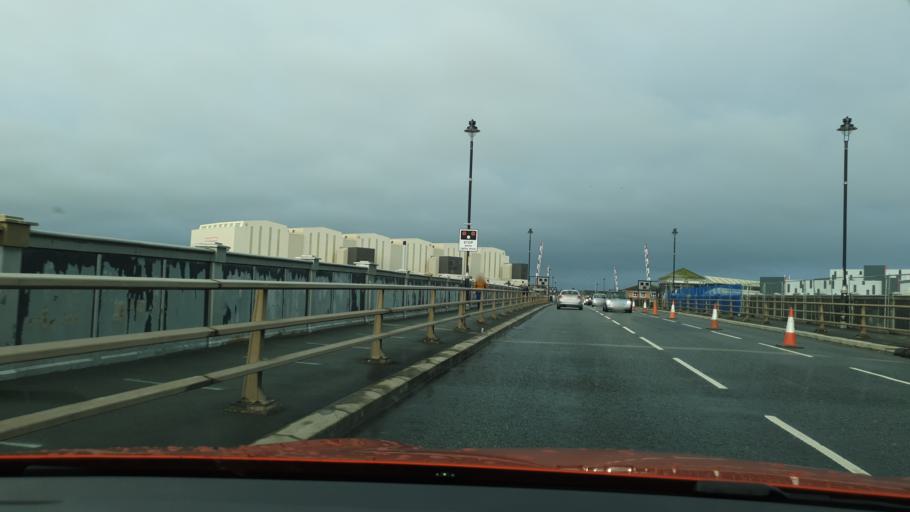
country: GB
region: England
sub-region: Cumbria
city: Barrow in Furness
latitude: 54.1074
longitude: -3.2449
